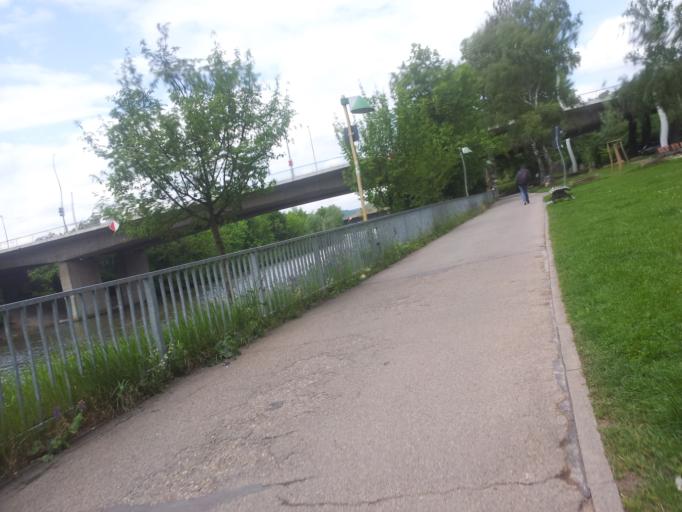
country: DE
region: Baden-Wuerttemberg
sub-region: Regierungsbezirk Stuttgart
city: Esslingen
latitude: 48.7358
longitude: 9.3067
